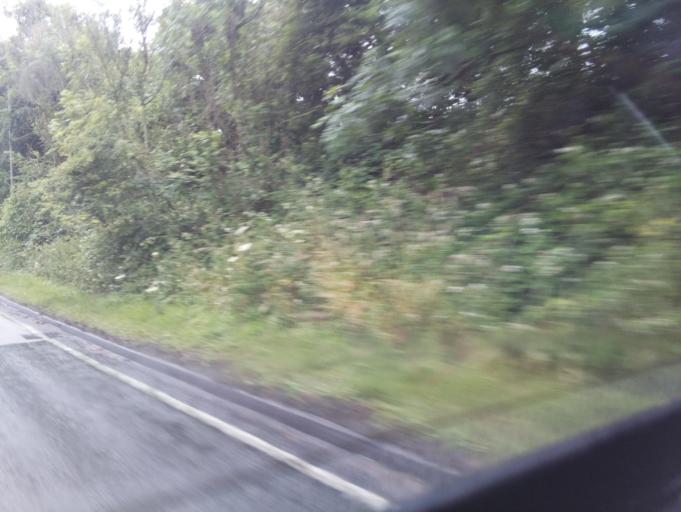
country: GB
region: England
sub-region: Surrey
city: Reigate
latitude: 51.2572
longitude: -0.1940
